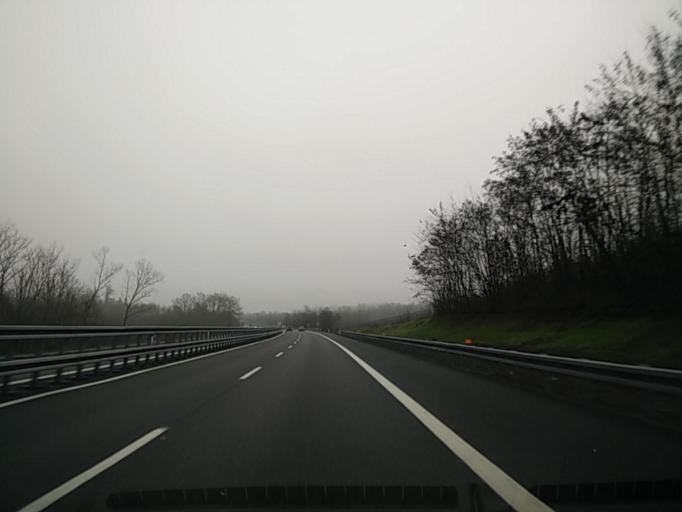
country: IT
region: Piedmont
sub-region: Provincia di Asti
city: Refrancore
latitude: 44.9048
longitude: 8.3435
